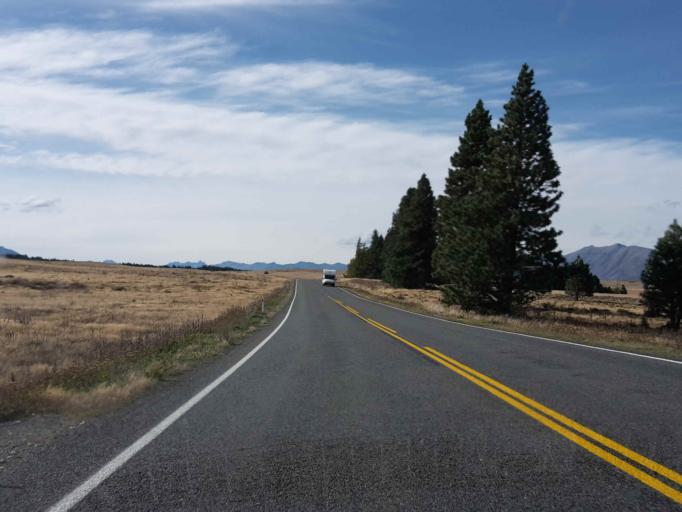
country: NZ
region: Canterbury
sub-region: Timaru District
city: Pleasant Point
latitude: -44.0300
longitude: 170.3947
